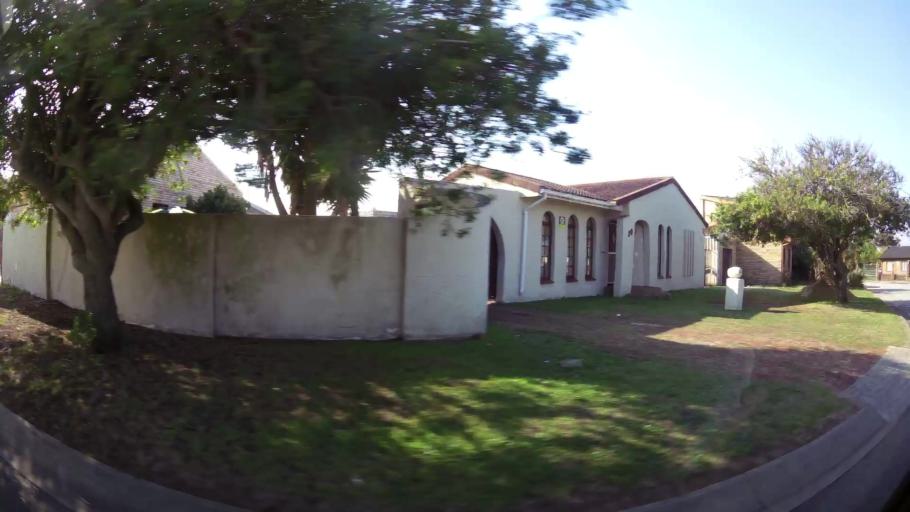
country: ZA
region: Eastern Cape
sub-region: Nelson Mandela Bay Metropolitan Municipality
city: Port Elizabeth
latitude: -33.9210
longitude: 25.5261
